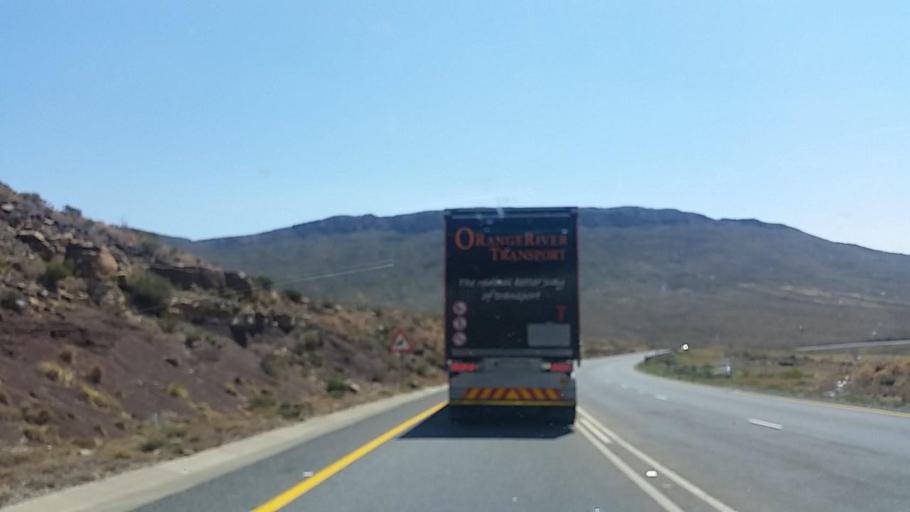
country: ZA
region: Eastern Cape
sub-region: Chris Hani District Municipality
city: Middelburg
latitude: -31.8238
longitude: 24.8555
